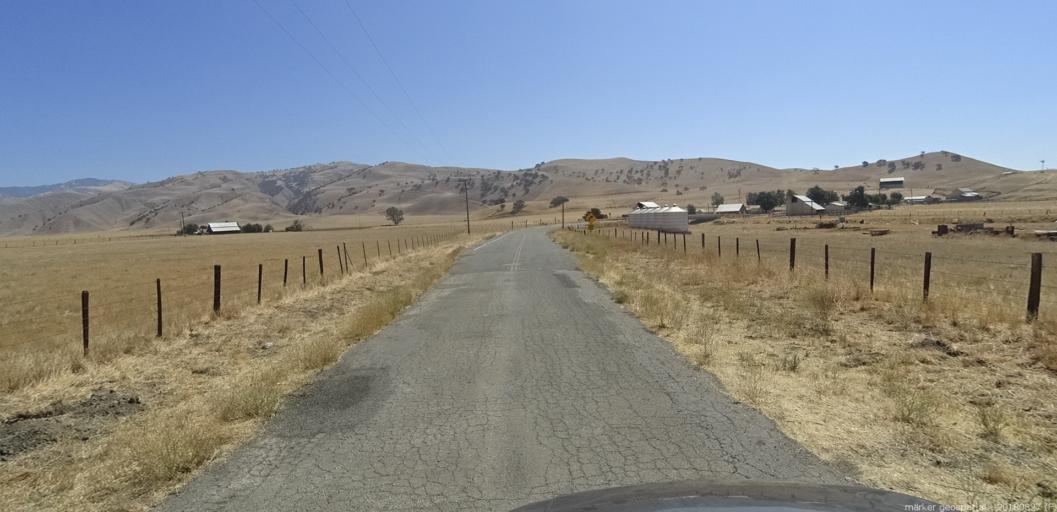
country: US
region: California
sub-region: Monterey County
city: King City
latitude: 36.2799
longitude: -120.9472
